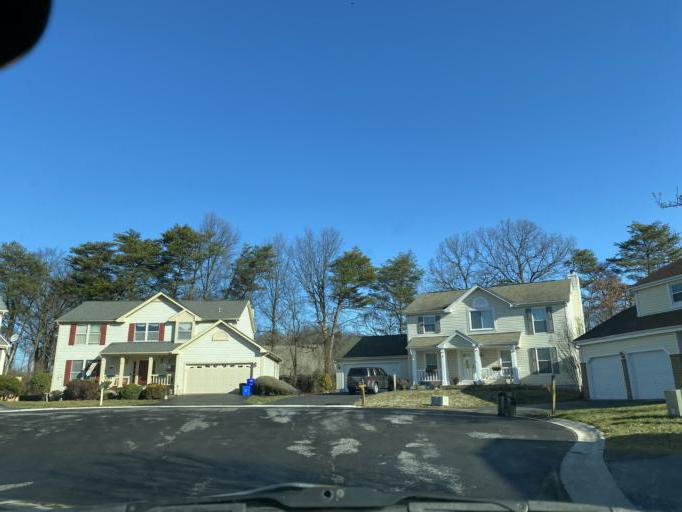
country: US
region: Maryland
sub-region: Montgomery County
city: Burtonsville
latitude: 39.1032
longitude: -76.9201
